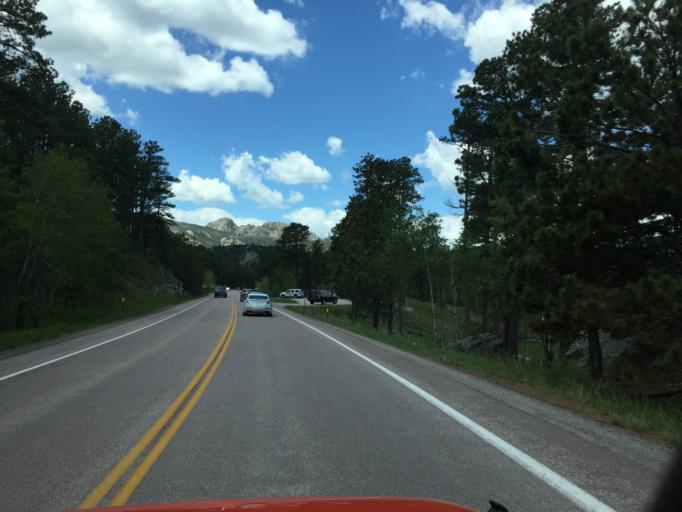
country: US
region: South Dakota
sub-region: Custer County
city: Custer
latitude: 43.8871
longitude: -103.4700
